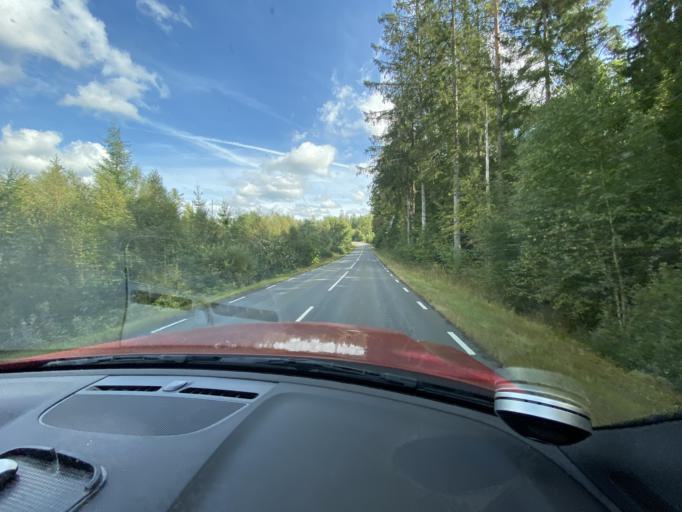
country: SE
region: Skane
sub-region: Hassleholms Kommun
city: Bjarnum
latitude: 56.3515
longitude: 13.7264
